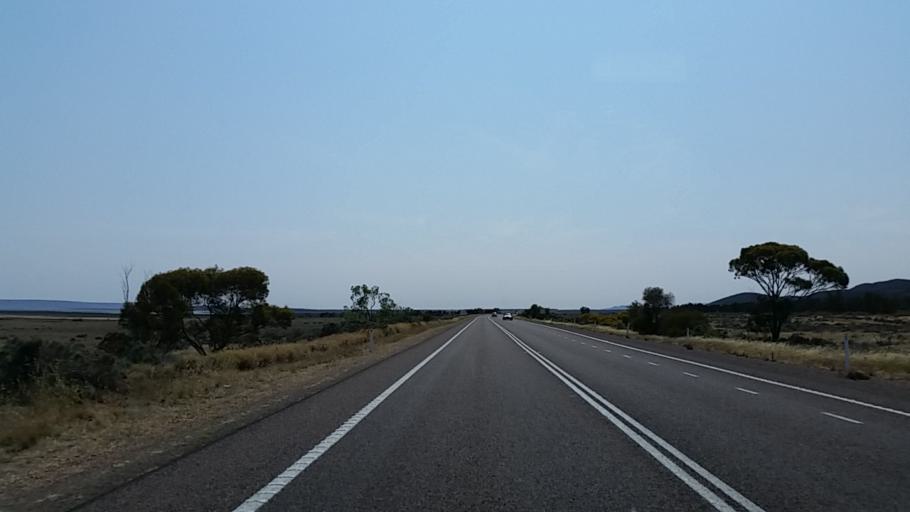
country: AU
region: South Australia
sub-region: Port Augusta
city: Port Augusta
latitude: -32.7869
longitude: 137.9563
